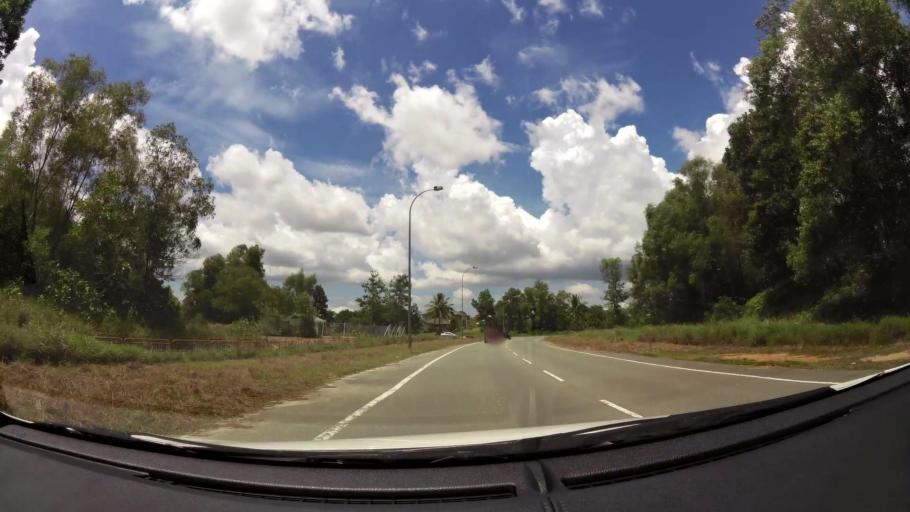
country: BN
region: Brunei and Muara
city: Bandar Seri Begawan
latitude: 4.9655
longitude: 114.9126
